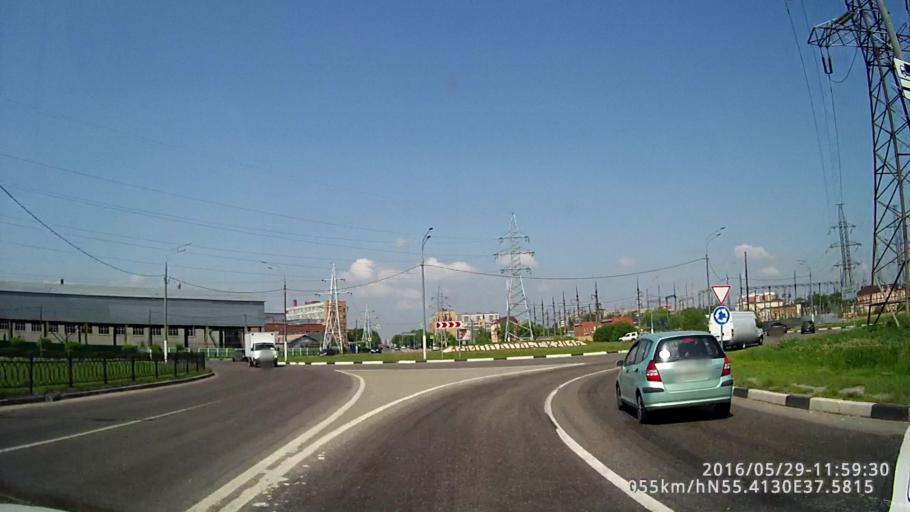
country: RU
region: Moskovskaya
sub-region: Podol'skiy Rayon
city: Podol'sk
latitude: 55.4132
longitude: 37.5811
